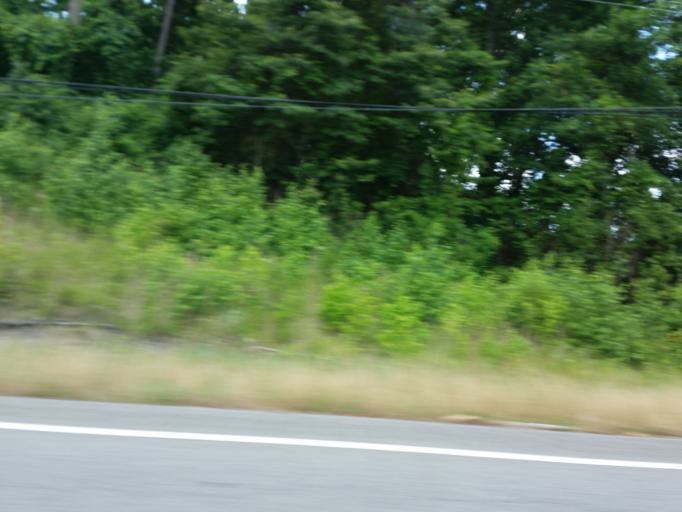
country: US
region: Alabama
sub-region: Sumter County
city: York
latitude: 32.4154
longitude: -88.2373
